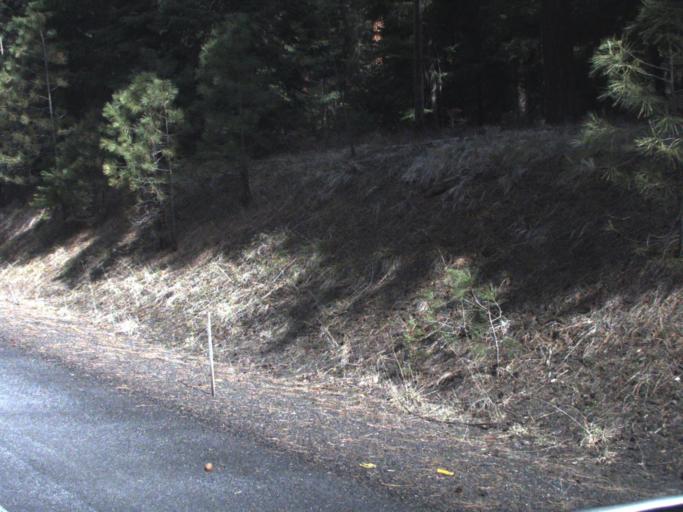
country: US
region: Washington
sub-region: Kittitas County
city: Cle Elum
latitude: 46.9218
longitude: -121.0476
